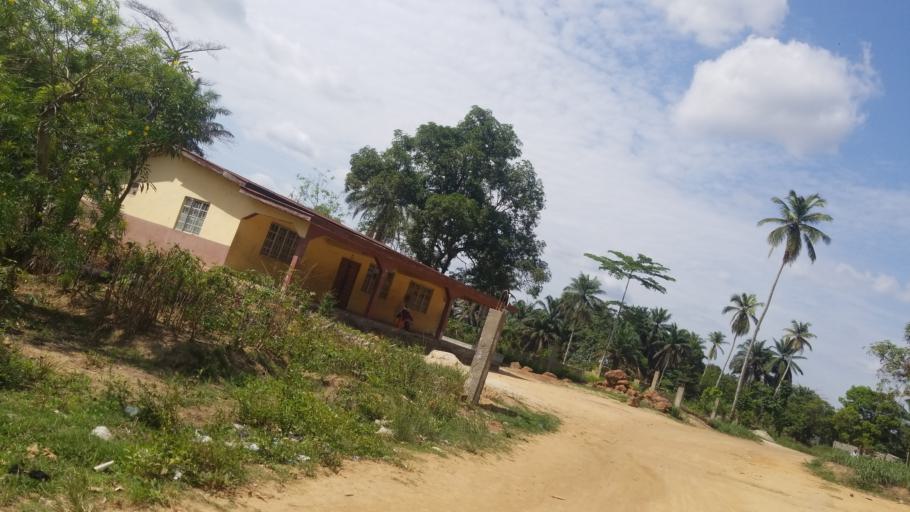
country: SL
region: Western Area
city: Waterloo
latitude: 8.3217
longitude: -13.0324
